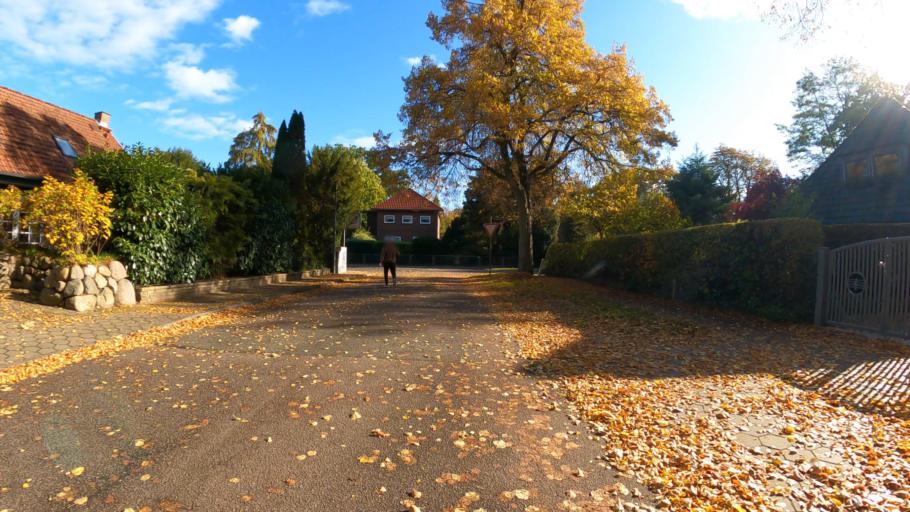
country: DE
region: Schleswig-Holstein
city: Ahrensburg
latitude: 53.6652
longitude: 10.2421
